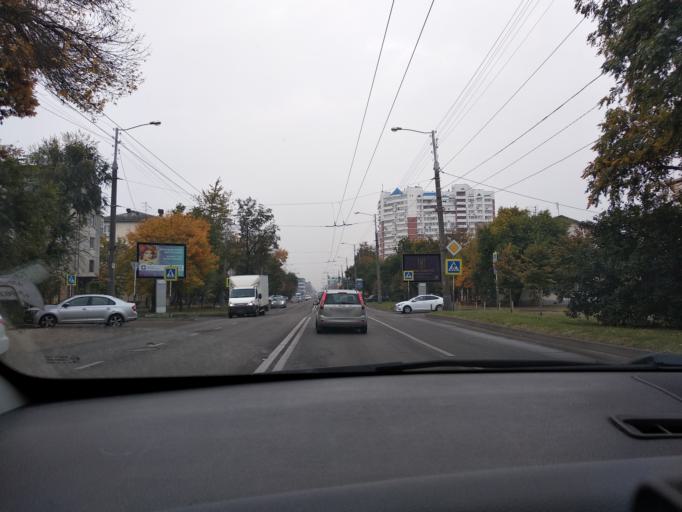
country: RU
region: Krasnodarskiy
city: Krasnodar
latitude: 45.0549
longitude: 38.9603
